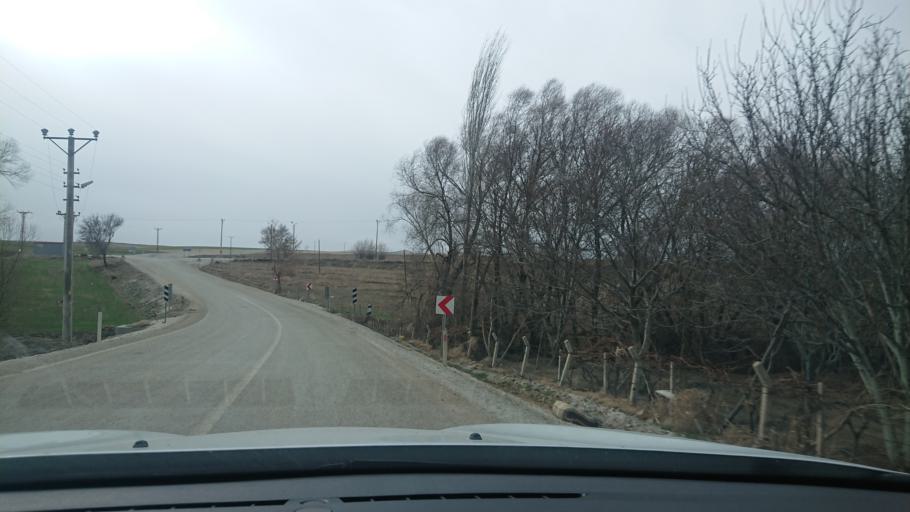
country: TR
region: Aksaray
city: Agacoren
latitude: 38.9252
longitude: 33.9498
